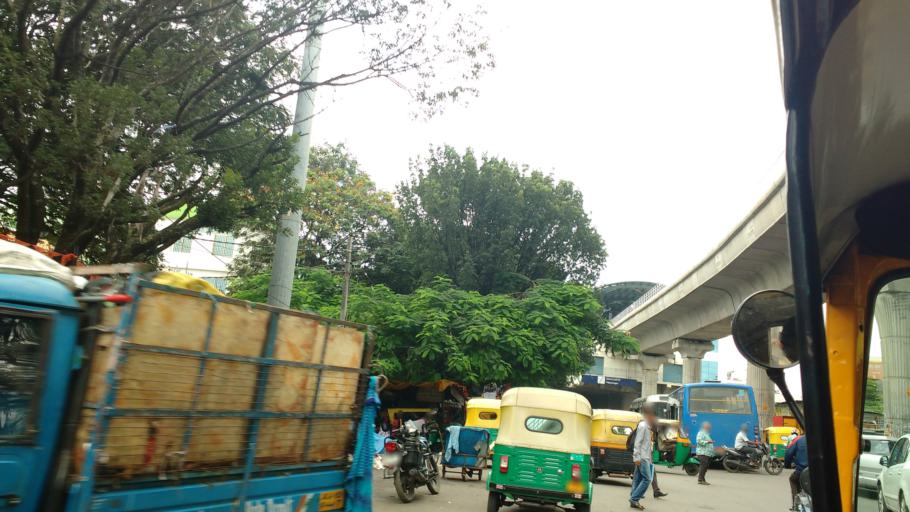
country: IN
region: Karnataka
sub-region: Bangalore Urban
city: Bangalore
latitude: 12.9723
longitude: 77.5381
